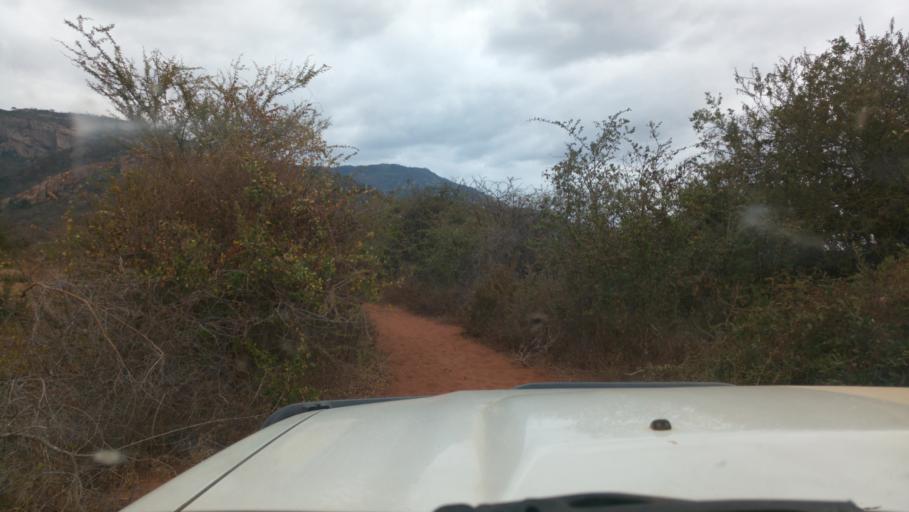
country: KE
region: Kitui
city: Kitui
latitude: -1.8987
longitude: 38.3931
